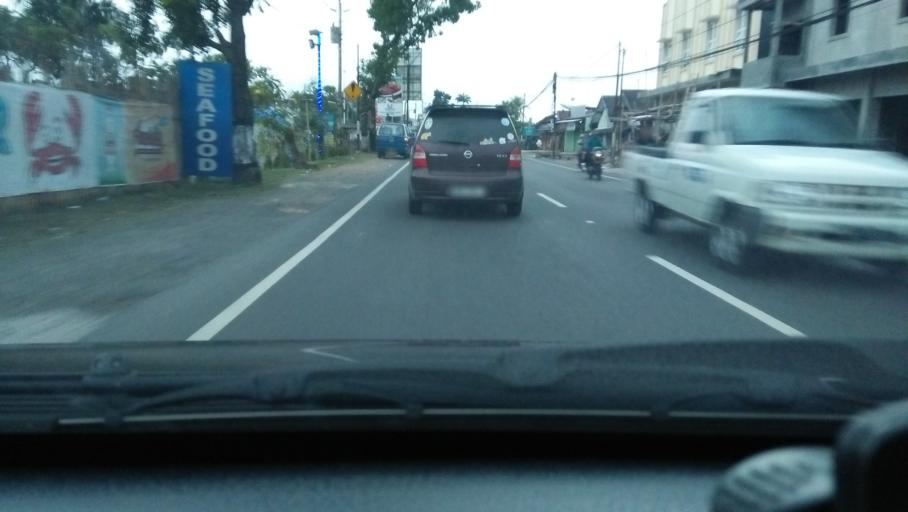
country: ID
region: Central Java
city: Magelang
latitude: -7.4323
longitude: 110.2288
